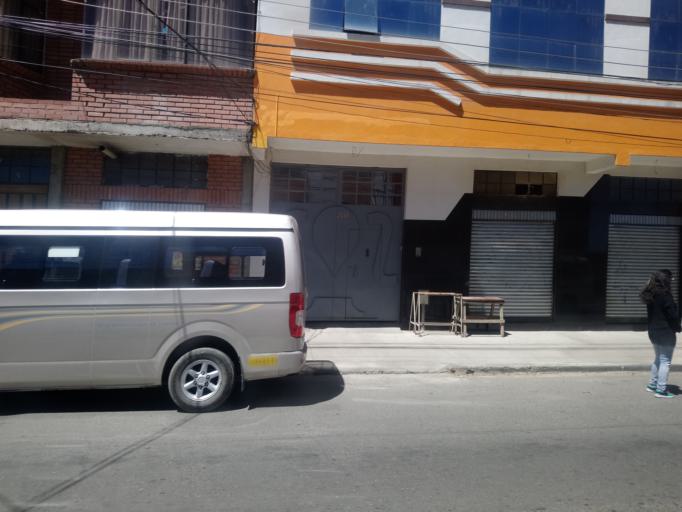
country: BO
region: La Paz
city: La Paz
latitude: -16.4939
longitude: -68.1140
